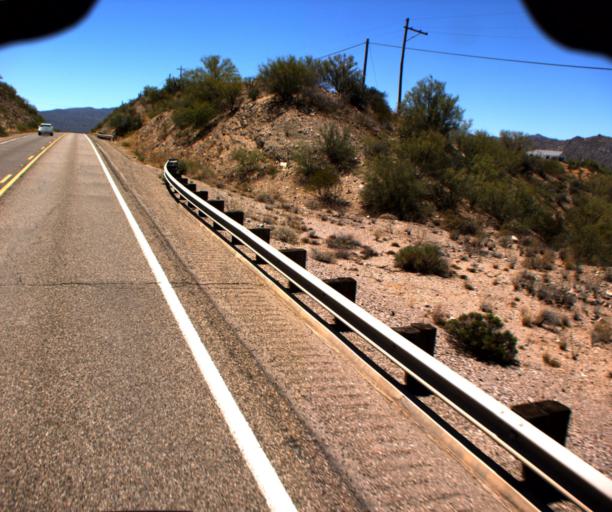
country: US
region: Arizona
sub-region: Pinal County
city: Kearny
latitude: 33.0860
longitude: -110.9274
